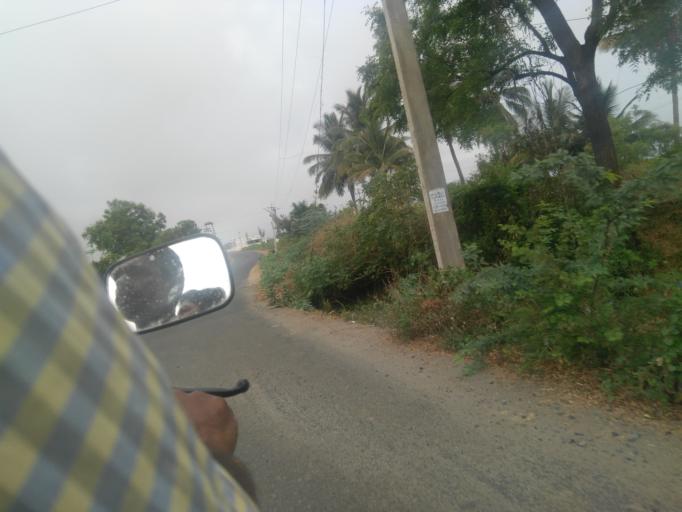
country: IN
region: Tamil Nadu
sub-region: Coimbatore
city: Karamadai
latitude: 11.2634
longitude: 76.9333
